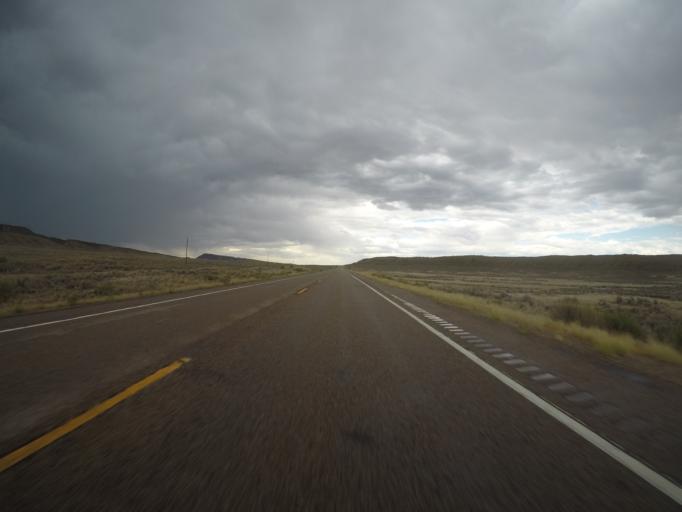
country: US
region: Colorado
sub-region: Rio Blanco County
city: Rangely
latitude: 40.2514
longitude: -108.8416
